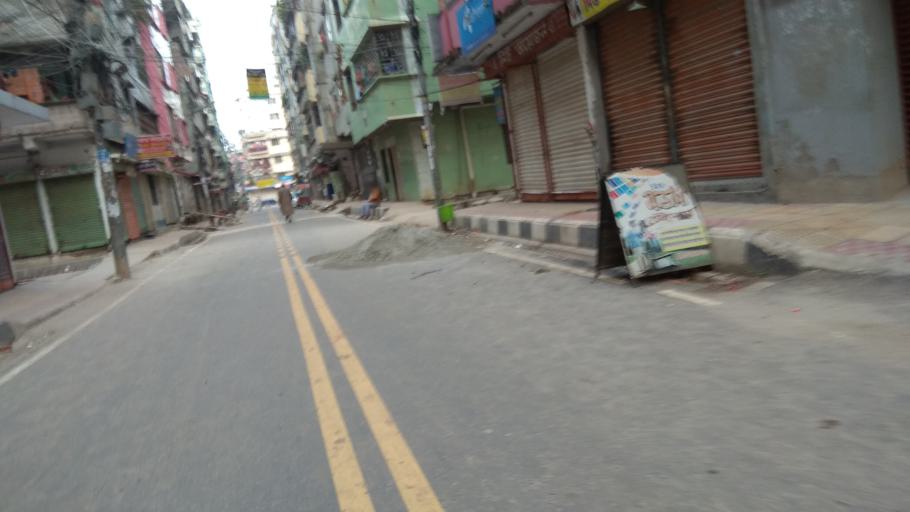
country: BD
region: Dhaka
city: Tungi
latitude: 23.8284
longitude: 90.3672
